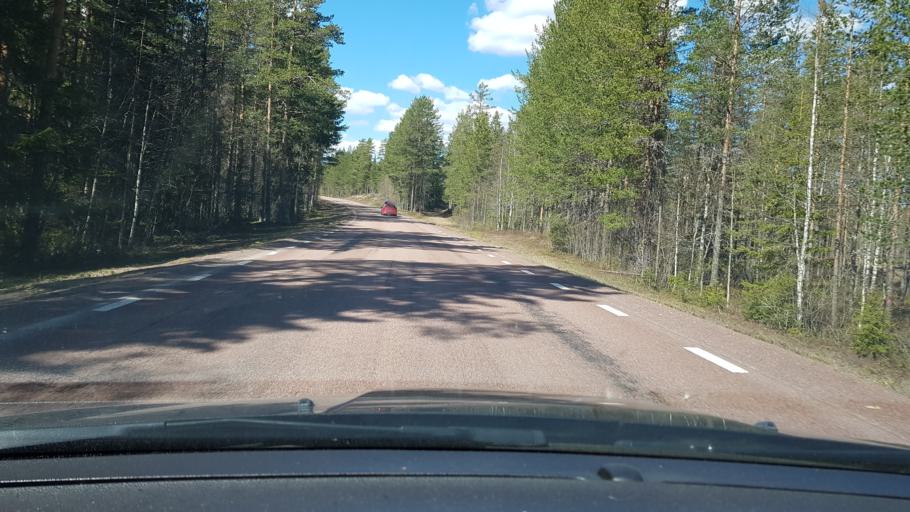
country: SE
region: Dalarna
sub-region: Alvdalens Kommun
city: AElvdalen
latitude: 61.1261
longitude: 14.0248
